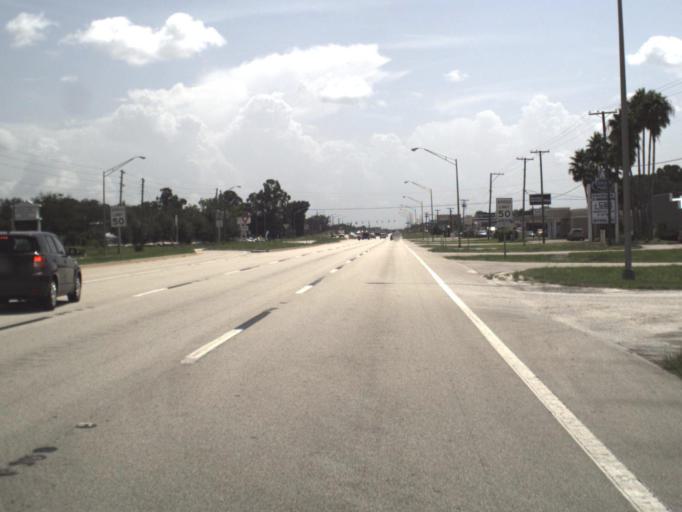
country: US
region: Florida
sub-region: Highlands County
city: Sebring
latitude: 27.4679
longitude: -81.4386
